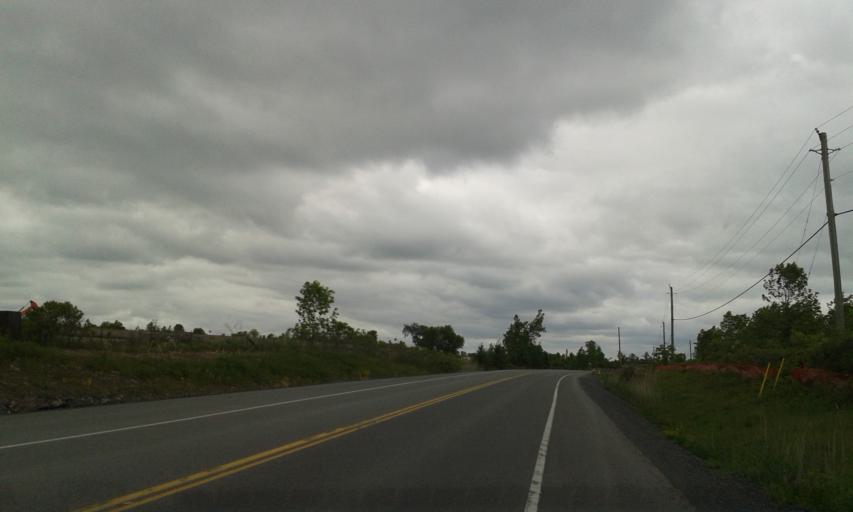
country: CA
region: Ontario
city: Skatepark
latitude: 44.1482
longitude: -76.8393
